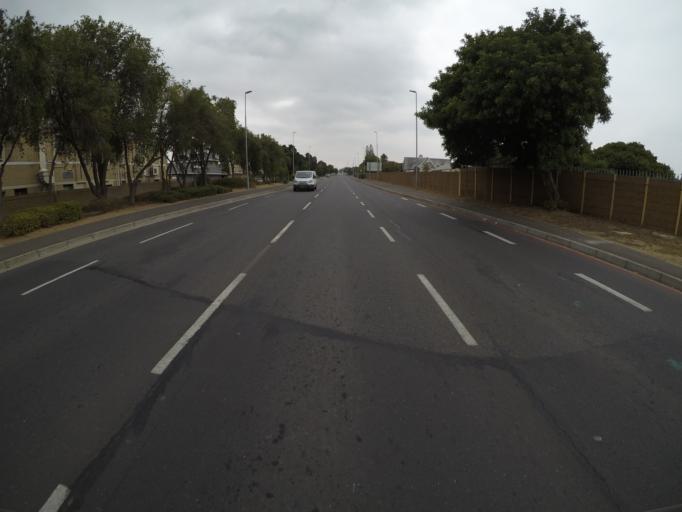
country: ZA
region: Western Cape
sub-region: City of Cape Town
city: Kraaifontein
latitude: -33.8765
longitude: 18.6375
